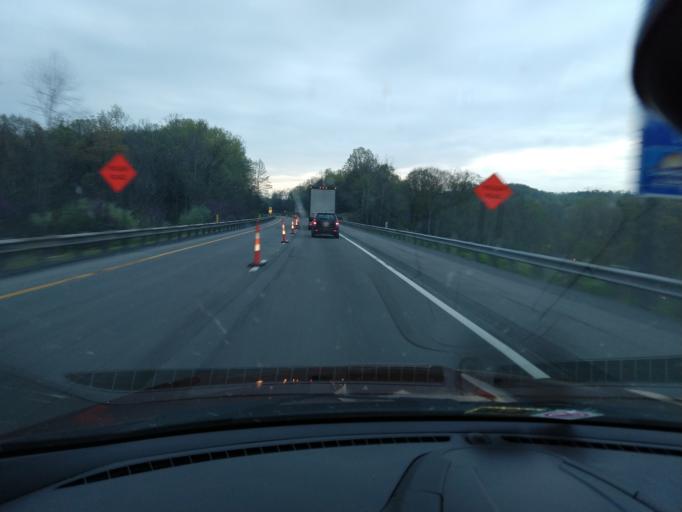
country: US
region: West Virginia
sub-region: Braxton County
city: Sutton
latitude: 38.6897
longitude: -80.6792
